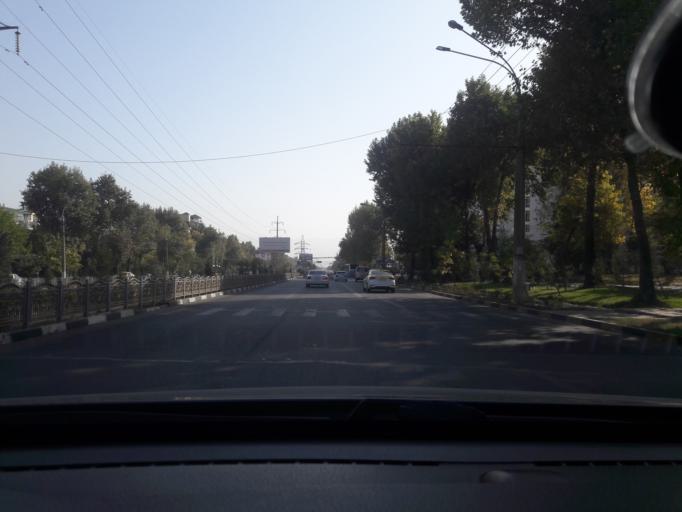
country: TJ
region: Dushanbe
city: Dushanbe
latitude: 38.5278
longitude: 68.7618
